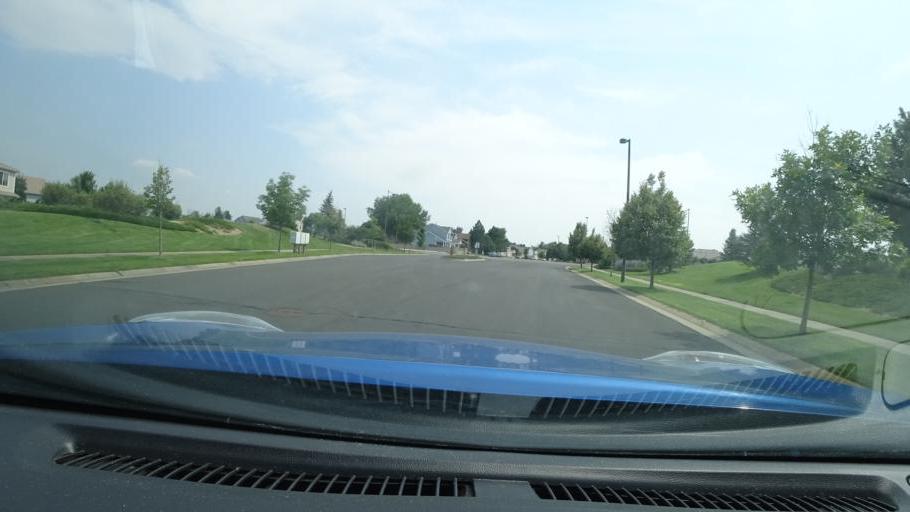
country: US
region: Colorado
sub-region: Adams County
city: Aurora
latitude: 39.7819
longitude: -104.7427
